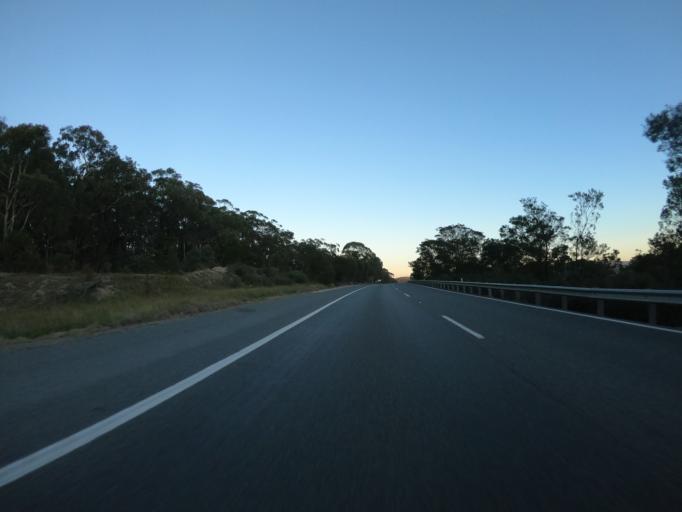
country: AU
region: New South Wales
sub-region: Goulburn Mulwaree
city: Goulburn
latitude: -34.7444
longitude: 149.9211
